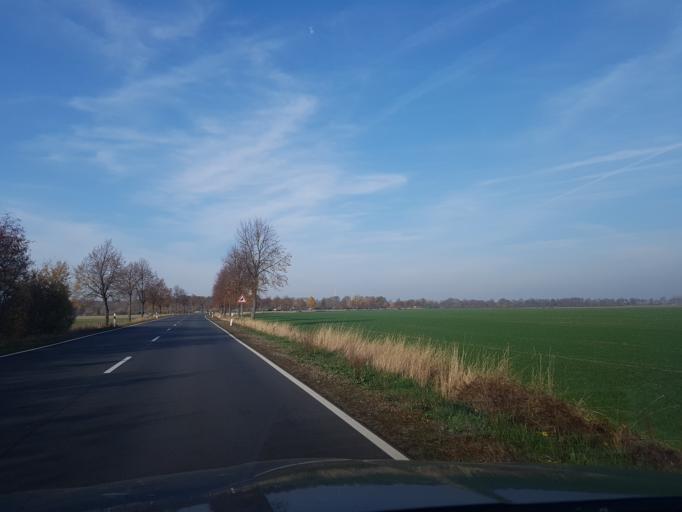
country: DE
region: Saxony
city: Torgau
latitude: 51.5556
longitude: 13.0285
